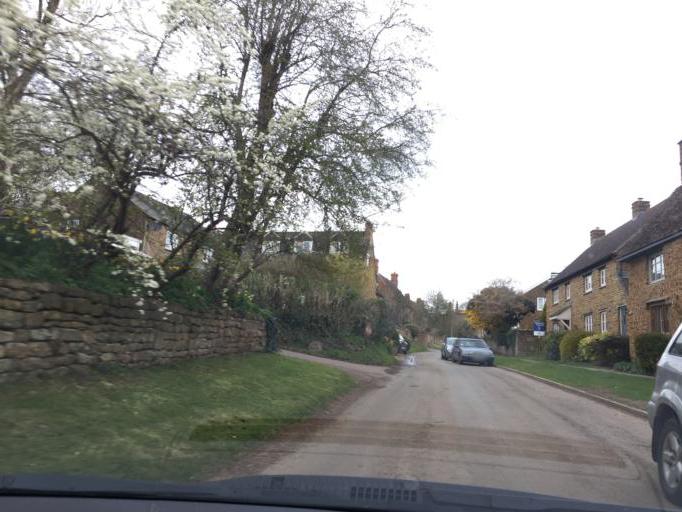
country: GB
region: England
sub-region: Oxfordshire
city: Hanwell
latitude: 52.0901
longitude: -1.3913
